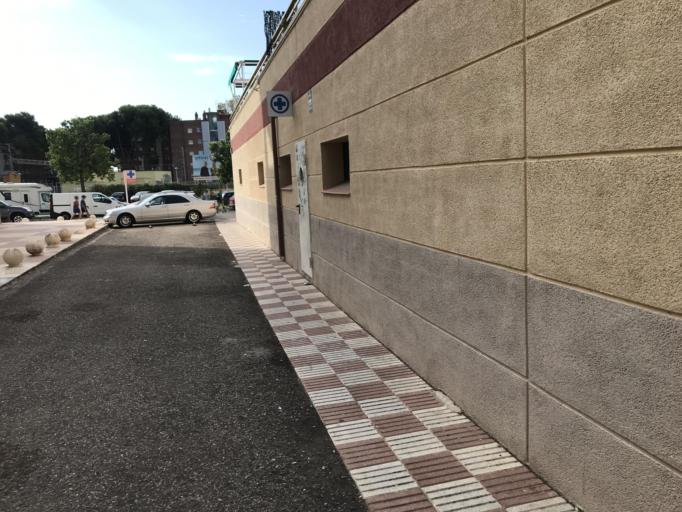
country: ES
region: Catalonia
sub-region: Provincia de Tarragona
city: Torredembarra
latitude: 41.1441
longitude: 1.4062
